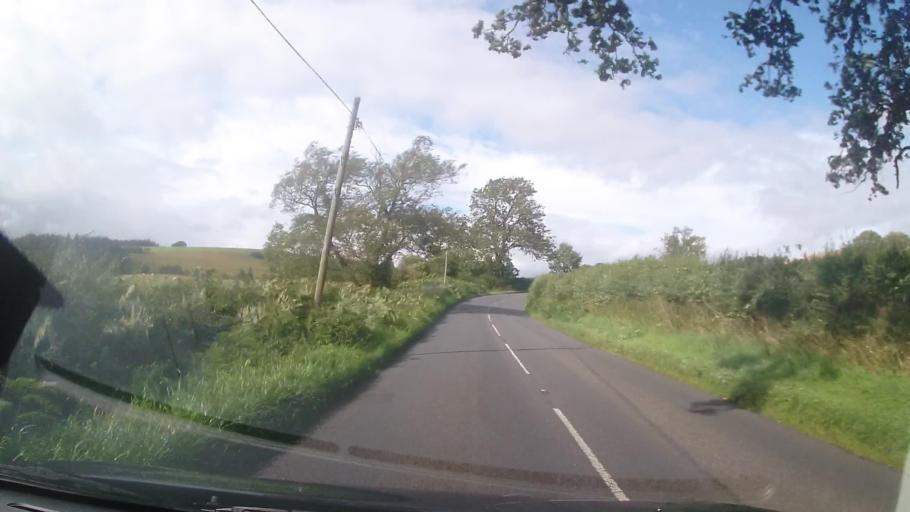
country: GB
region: England
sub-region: Shropshire
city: Acton
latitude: 52.4392
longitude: -3.0359
